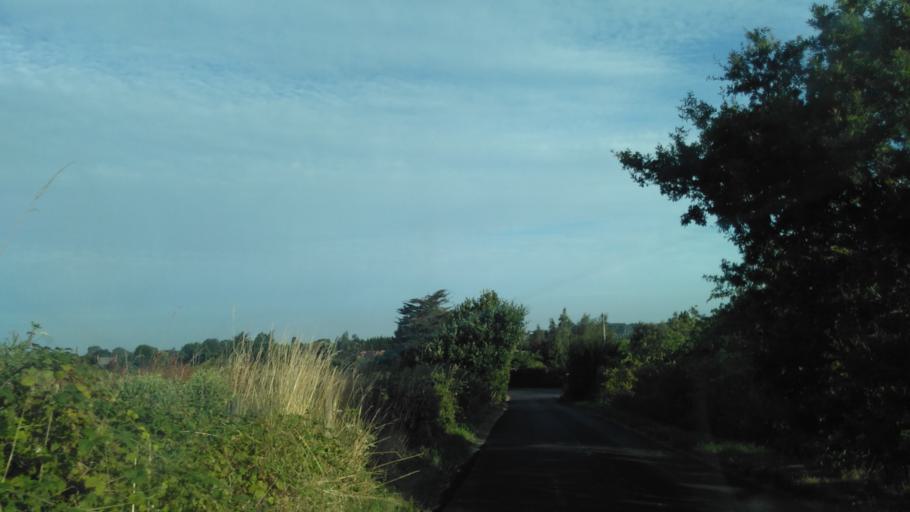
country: GB
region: England
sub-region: Kent
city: Dunkirk
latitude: 51.3139
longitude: 0.9905
